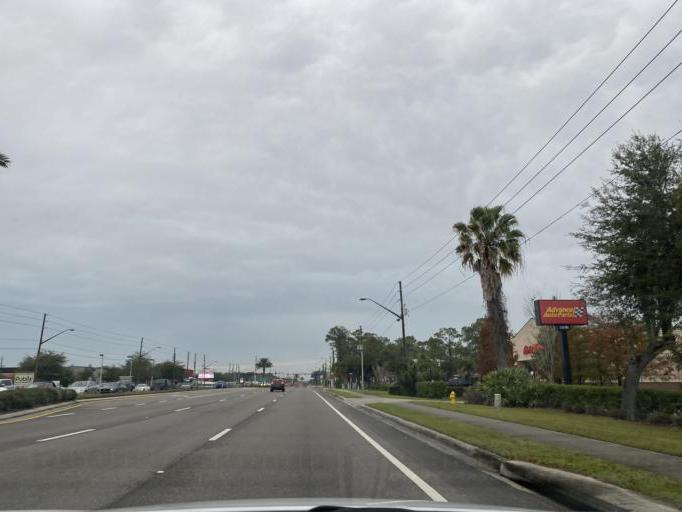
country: US
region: Florida
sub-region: Orange County
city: Winter Garden
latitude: 28.5511
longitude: -81.5886
